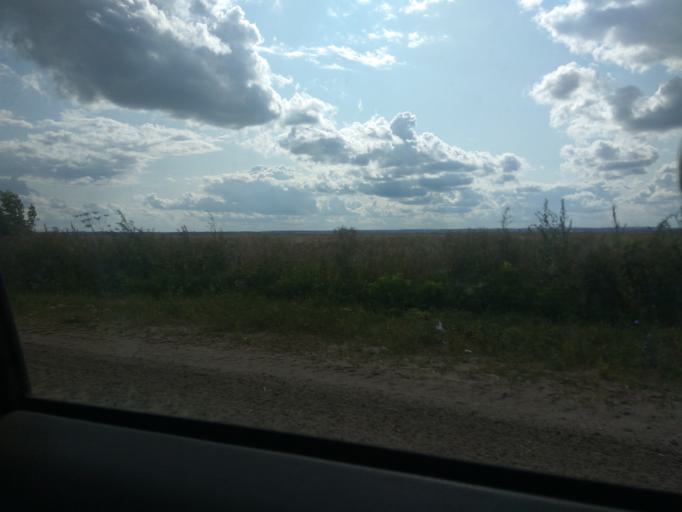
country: RU
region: Moskovskaya
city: Ramenskoye
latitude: 55.5345
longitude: 38.2778
